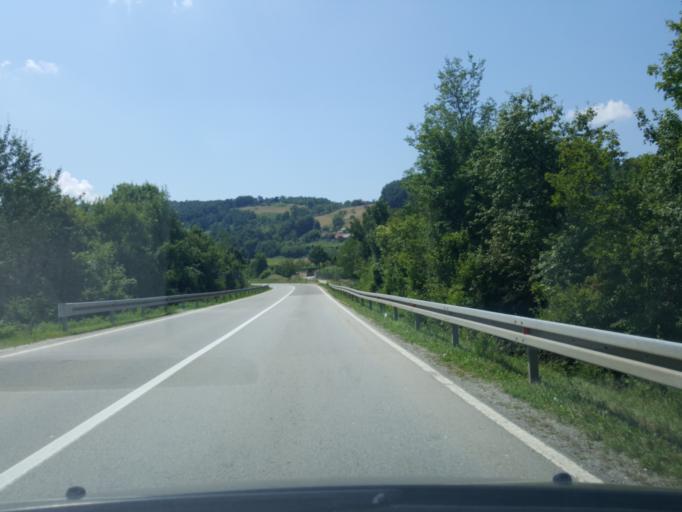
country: RS
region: Central Serbia
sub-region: Moravicki Okrug
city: Gornji Milanovac
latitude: 44.0911
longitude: 20.4800
